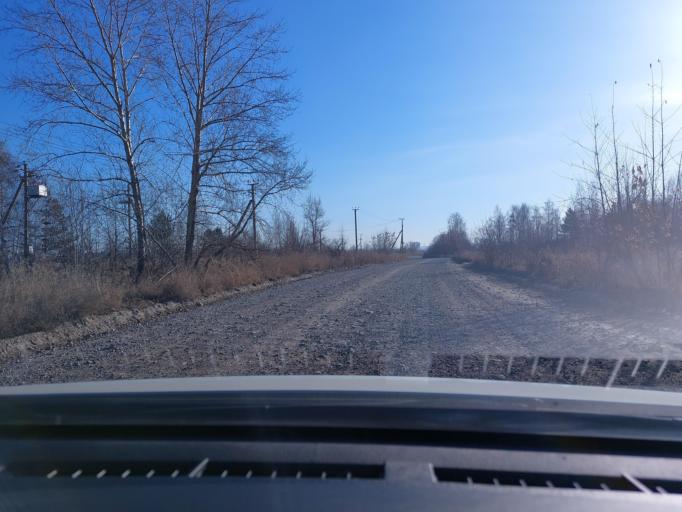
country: RU
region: Irkutsk
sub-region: Irkutskiy Rayon
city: Irkutsk
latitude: 52.3066
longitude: 104.2737
